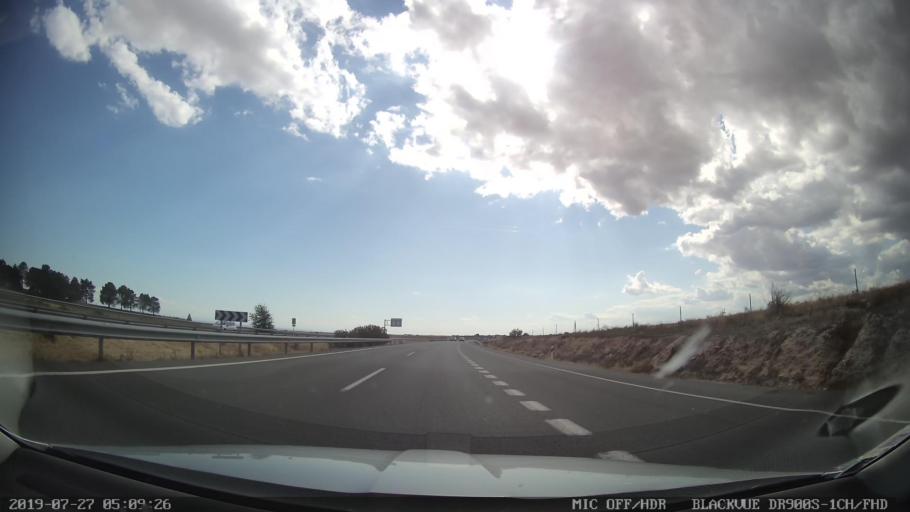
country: ES
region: Castille-La Mancha
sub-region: Province of Toledo
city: Santa Cruz del Retamar
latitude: 40.1195
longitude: -4.2647
